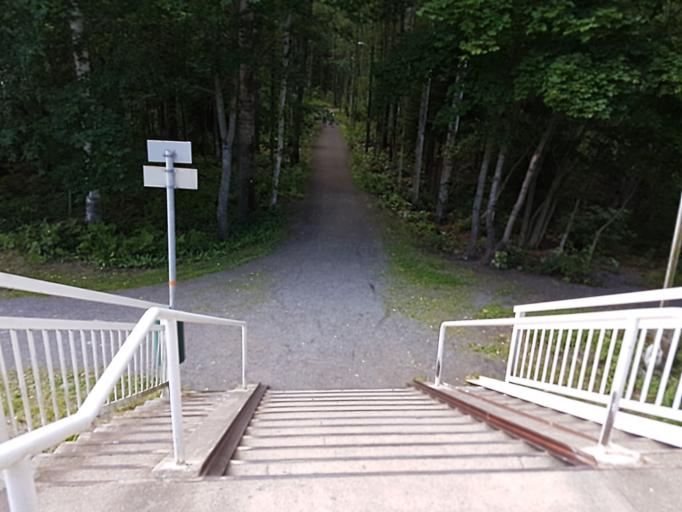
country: FI
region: Pirkanmaa
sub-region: Etelae-Pirkanmaa
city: Valkeakoski
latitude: 61.2726
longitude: 24.0470
